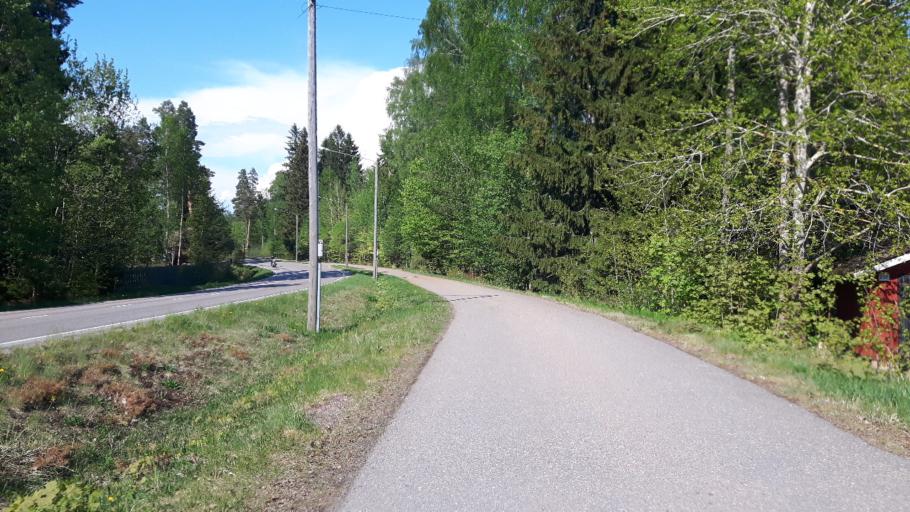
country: FI
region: Kymenlaakso
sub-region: Kotka-Hamina
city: Broby
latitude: 60.4940
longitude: 26.7705
